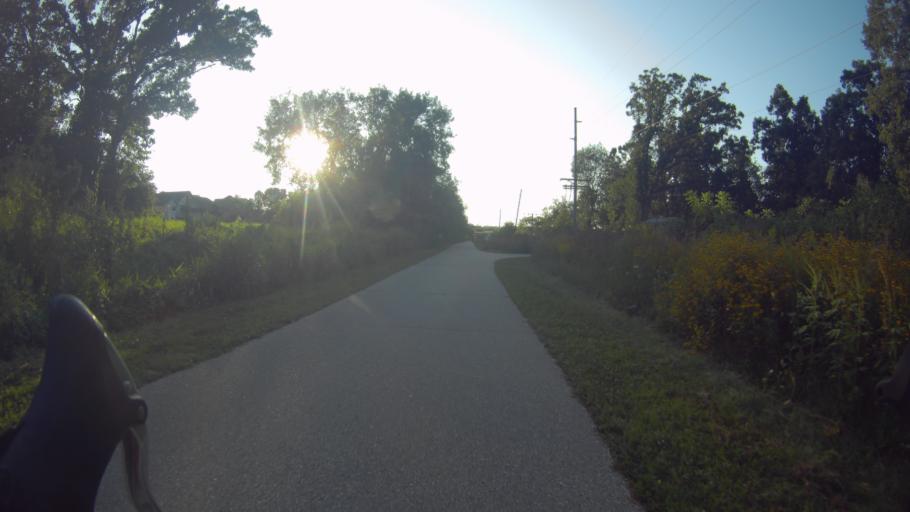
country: US
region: Wisconsin
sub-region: Dane County
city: Shorewood Hills
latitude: 43.0247
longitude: -89.4351
